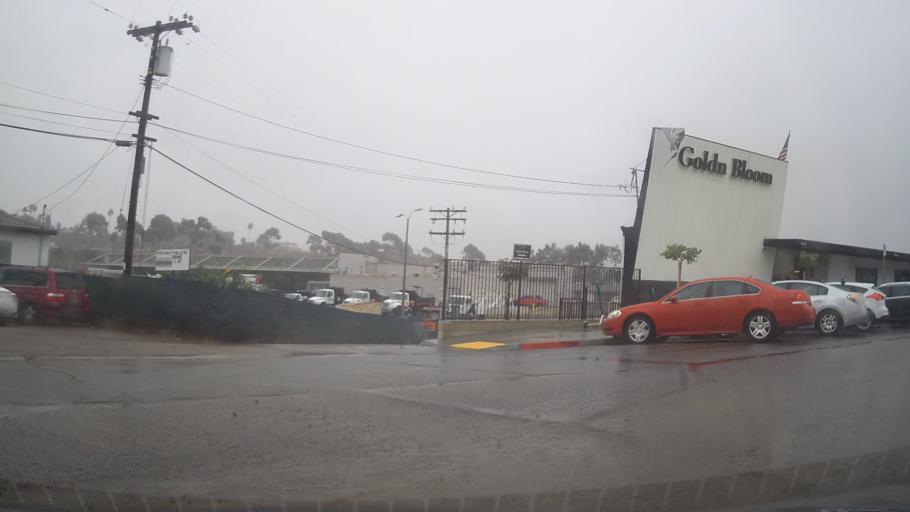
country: US
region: California
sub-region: San Diego County
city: San Diego
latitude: 32.7144
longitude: -117.1212
